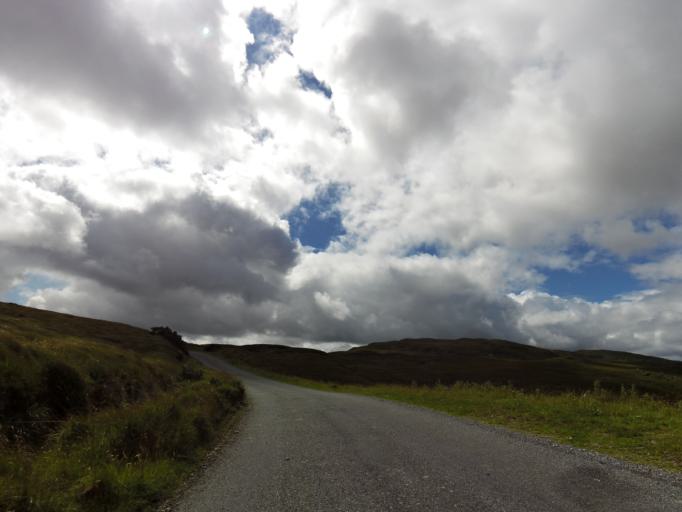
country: IE
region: Connaught
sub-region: County Galway
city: Oughterard
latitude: 53.3976
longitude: -9.3333
